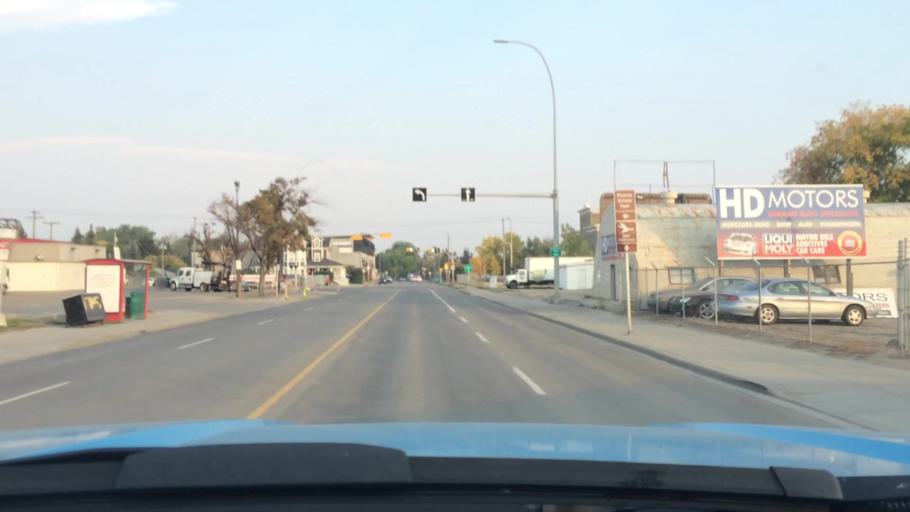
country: CA
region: Alberta
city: Calgary
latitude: 51.0360
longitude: -114.0213
